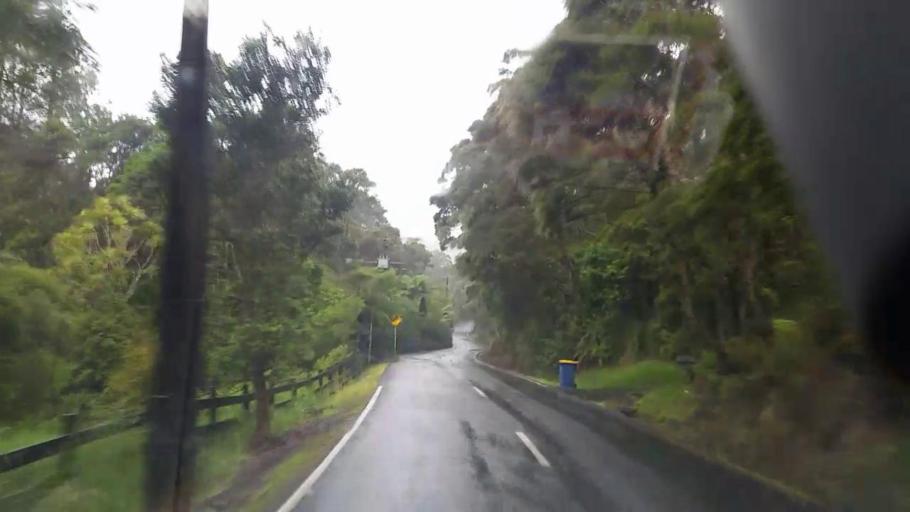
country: NZ
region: Auckland
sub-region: Auckland
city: Waitakere
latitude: -36.9056
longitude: 174.5702
